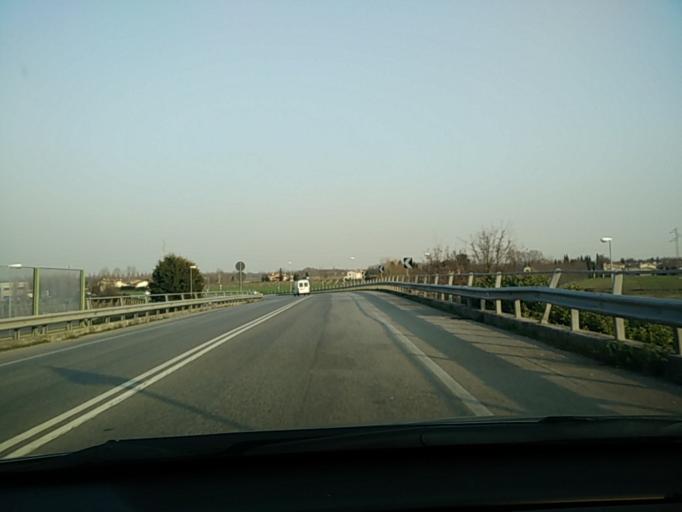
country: IT
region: Veneto
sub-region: Provincia di Treviso
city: Varago
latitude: 45.7415
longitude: 12.3146
